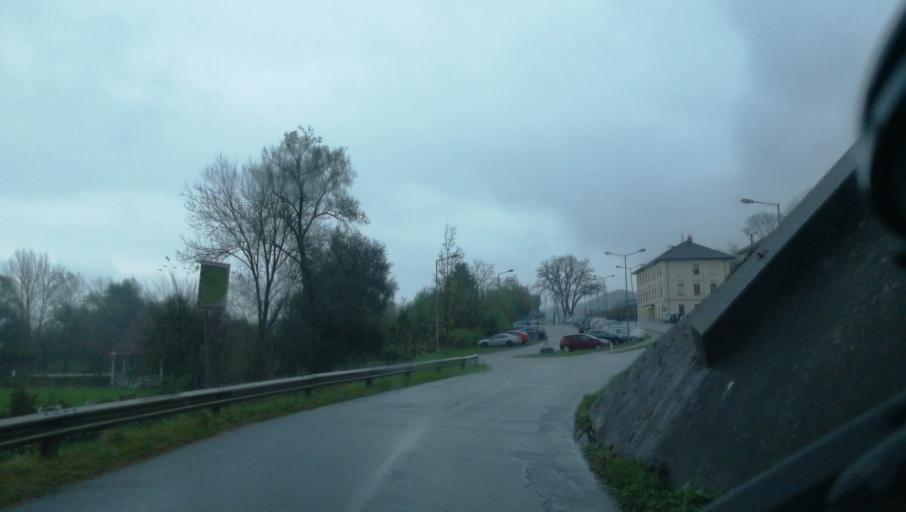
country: AT
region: Styria
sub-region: Politischer Bezirk Leibnitz
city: Spielfeld
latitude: 46.7110
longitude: 15.6278
